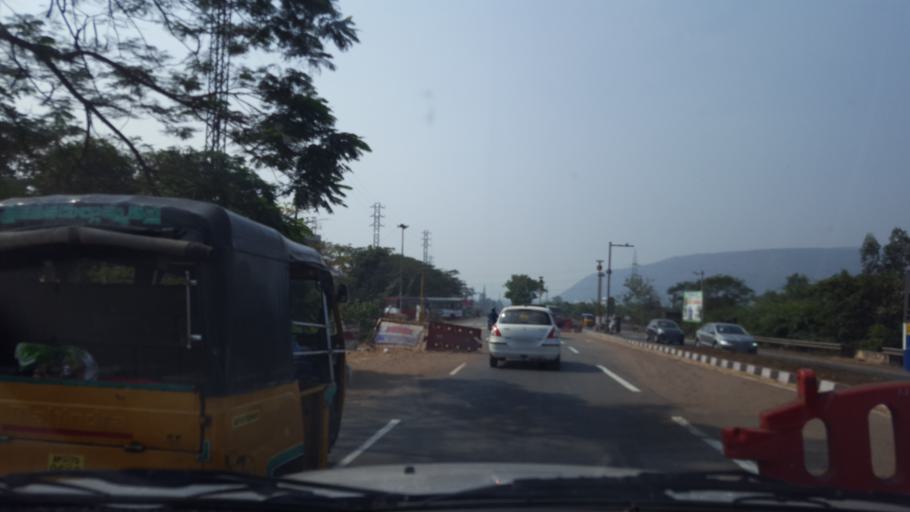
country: IN
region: Andhra Pradesh
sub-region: Vishakhapatnam
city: Bhimunipatnam
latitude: 17.8828
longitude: 83.3764
